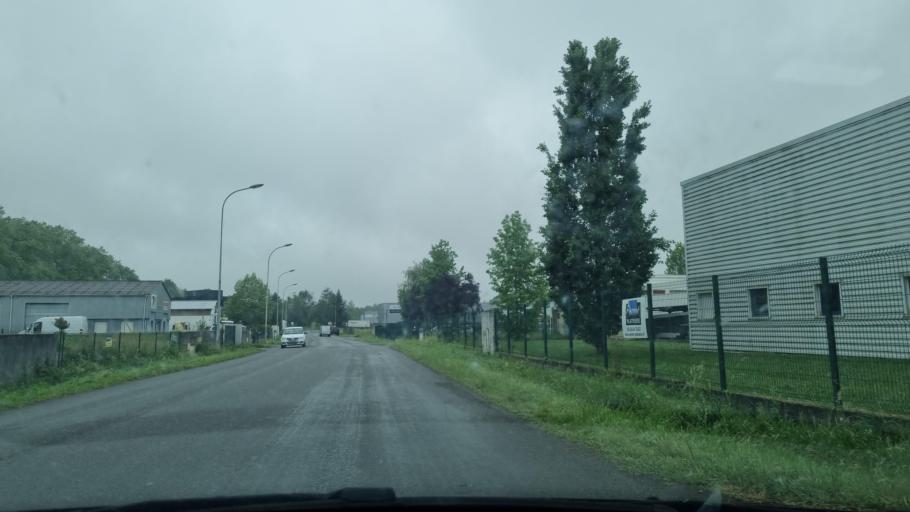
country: FR
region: Aquitaine
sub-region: Departement des Pyrenees-Atlantiques
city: Idron
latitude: 43.3194
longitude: -0.3245
